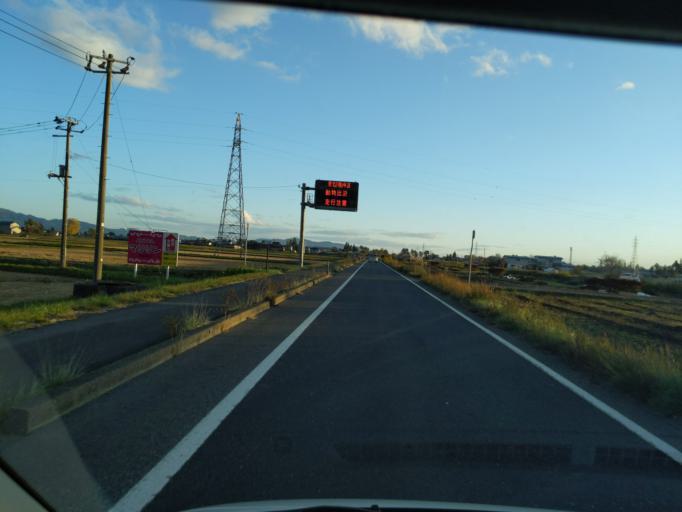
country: JP
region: Iwate
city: Mizusawa
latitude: 39.1798
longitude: 141.1216
